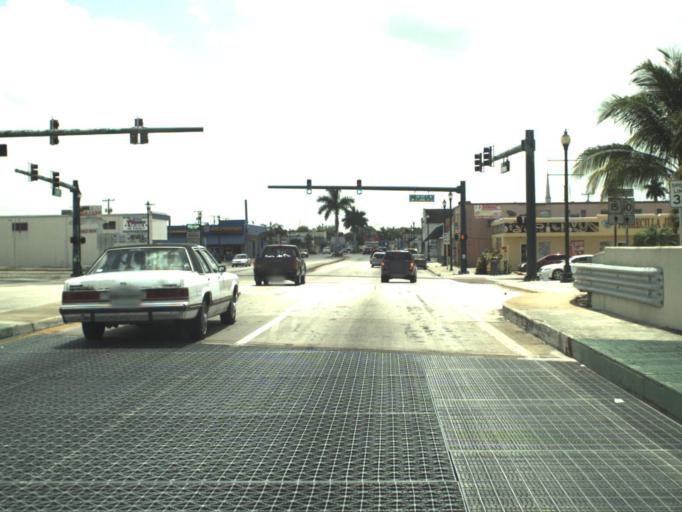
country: US
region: Florida
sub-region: Palm Beach County
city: Belle Glade
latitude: 26.6863
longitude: -80.6679
